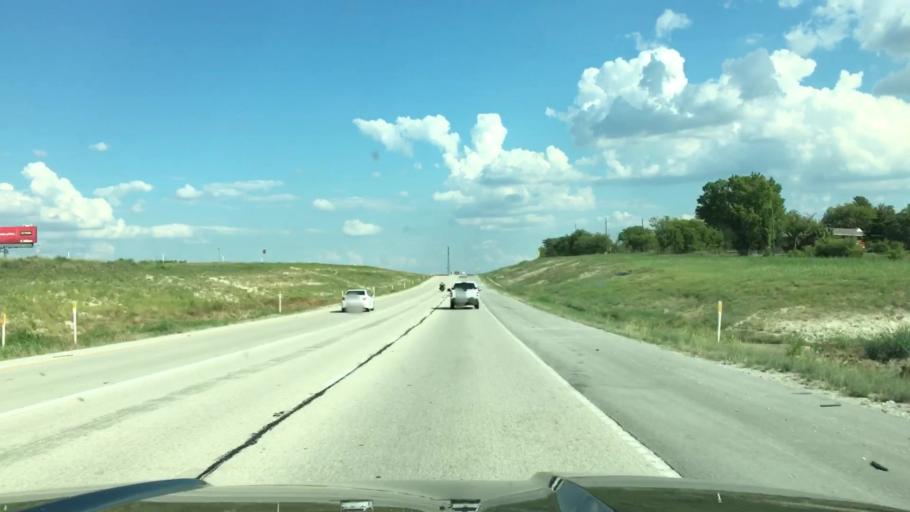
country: US
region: Texas
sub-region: Wise County
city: New Fairview
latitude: 33.1514
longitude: -97.5105
